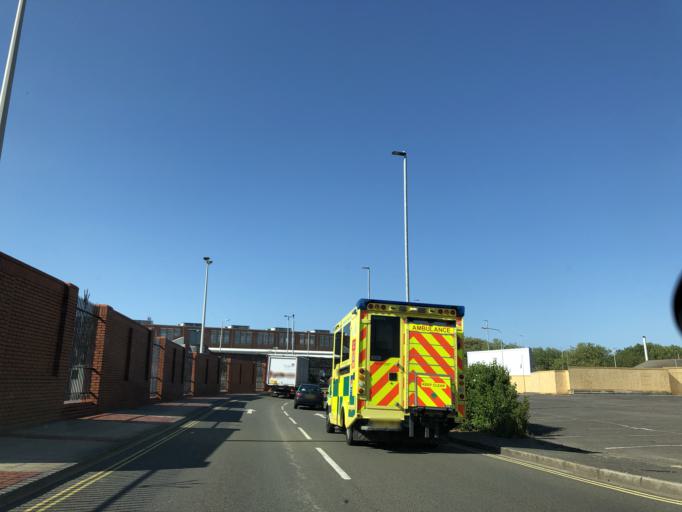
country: GB
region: England
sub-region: Portsmouth
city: Portsmouth
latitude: 50.8034
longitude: -1.0908
